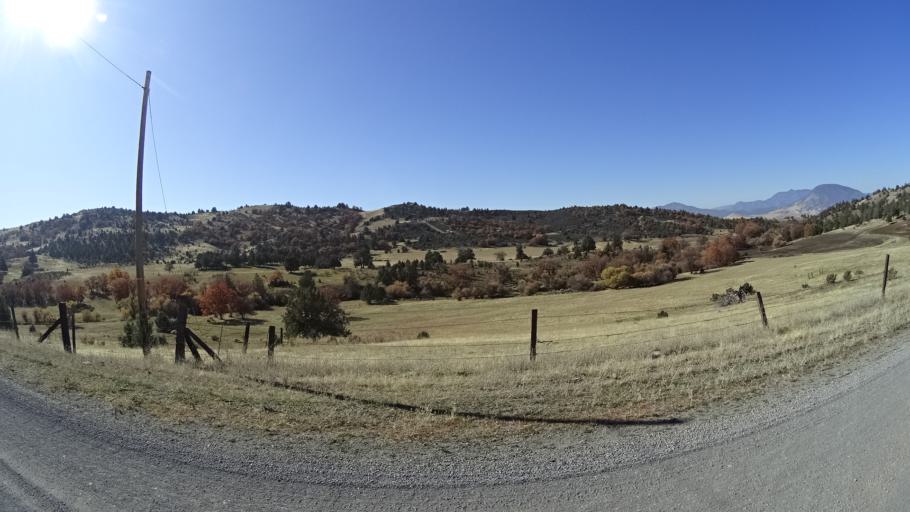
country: US
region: California
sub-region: Siskiyou County
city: Montague
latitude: 41.7988
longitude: -122.3676
